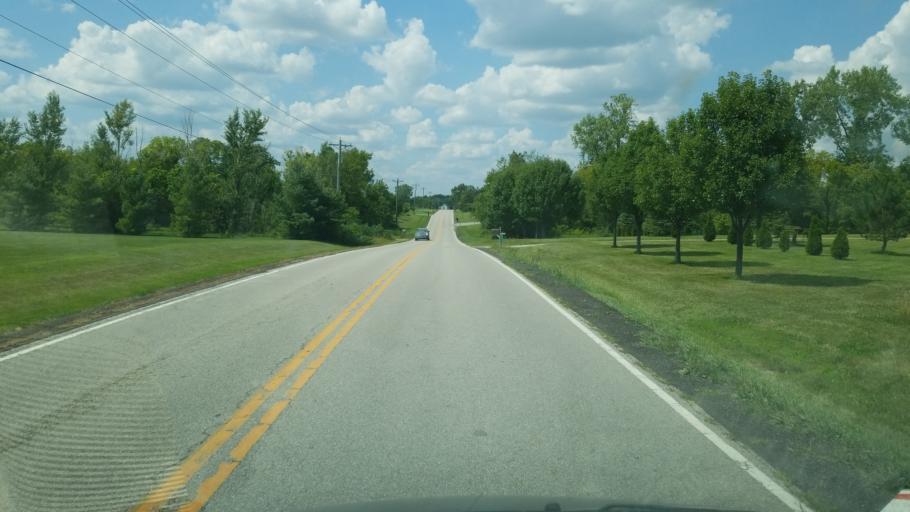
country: US
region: Ohio
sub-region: Union County
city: Marysville
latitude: 40.2884
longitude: -83.4664
